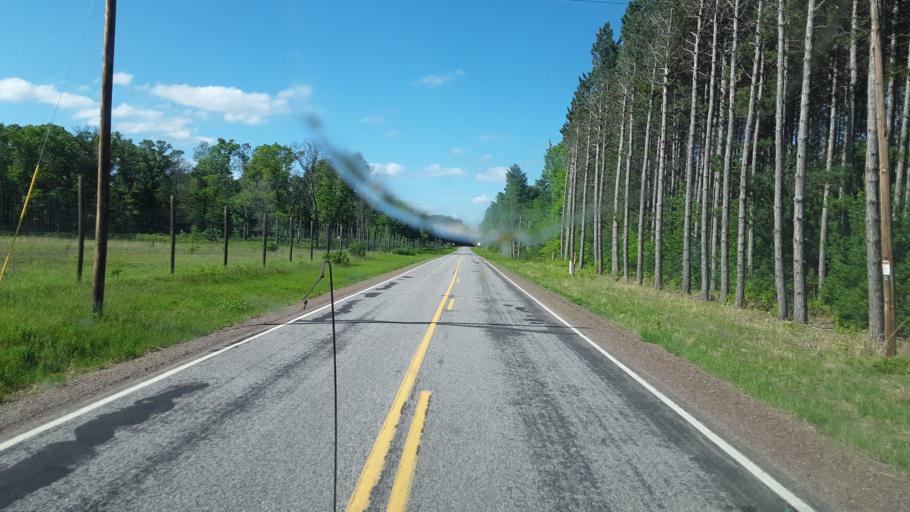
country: US
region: Wisconsin
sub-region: Wood County
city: Nekoosa
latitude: 44.3095
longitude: -90.1295
